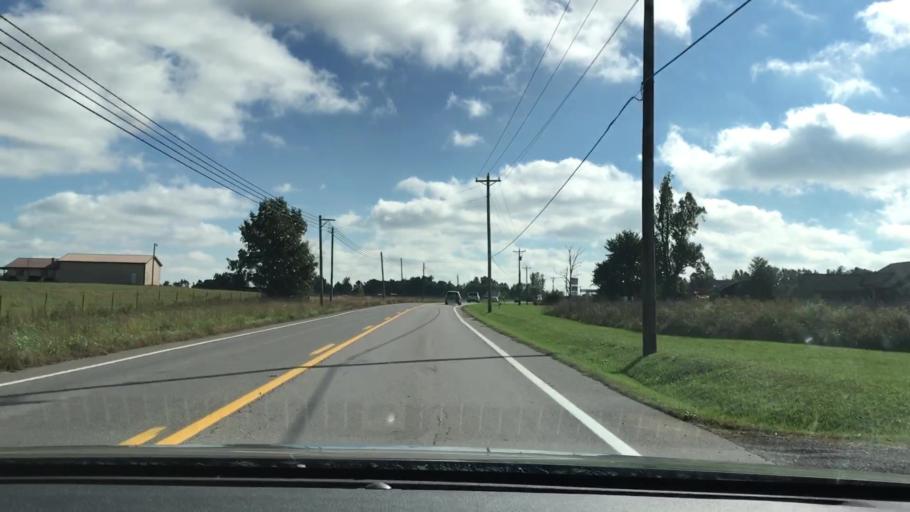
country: US
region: Tennessee
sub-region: Fentress County
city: Grimsley
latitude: 36.2145
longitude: -85.0141
